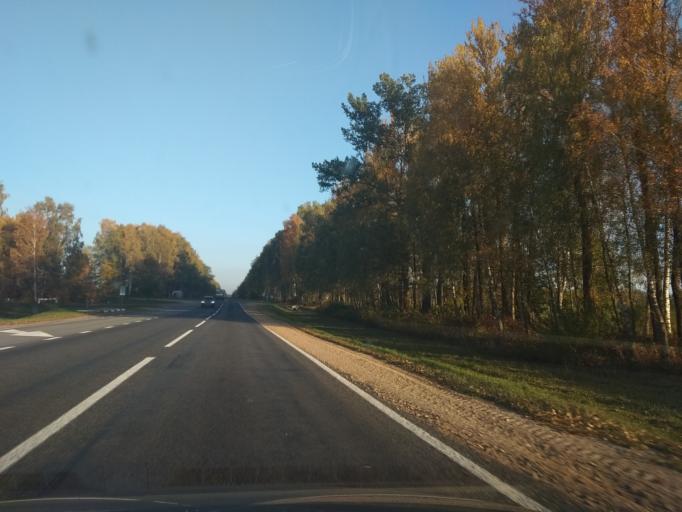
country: BY
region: Grodnenskaya
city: Vawkavysk
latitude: 53.1499
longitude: 24.5641
